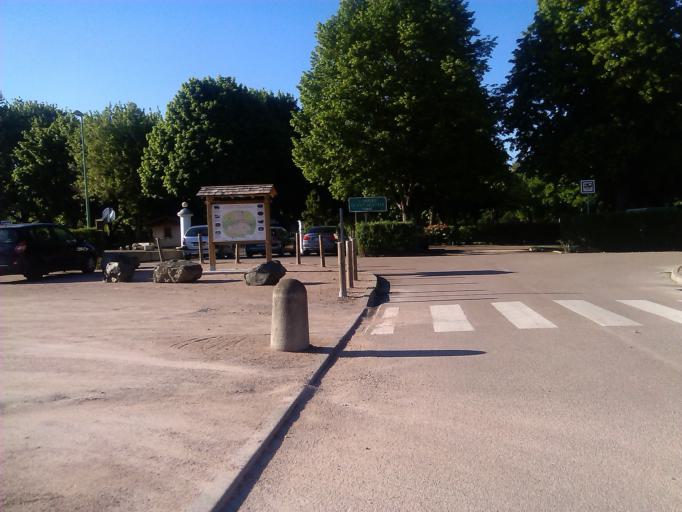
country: FR
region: Auvergne
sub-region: Departement de l'Allier
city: Diou
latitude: 46.5349
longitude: 3.7440
